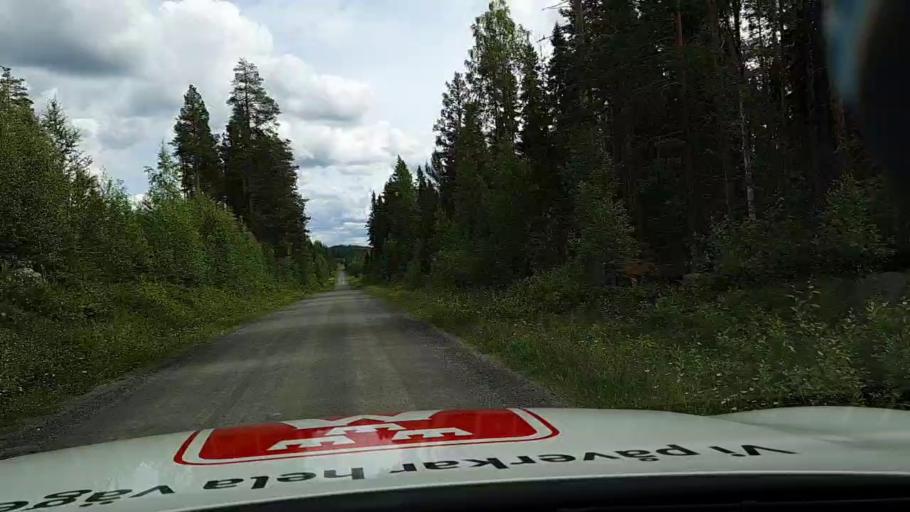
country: SE
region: Jaemtland
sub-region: OEstersunds Kommun
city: Lit
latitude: 63.2907
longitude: 15.3497
